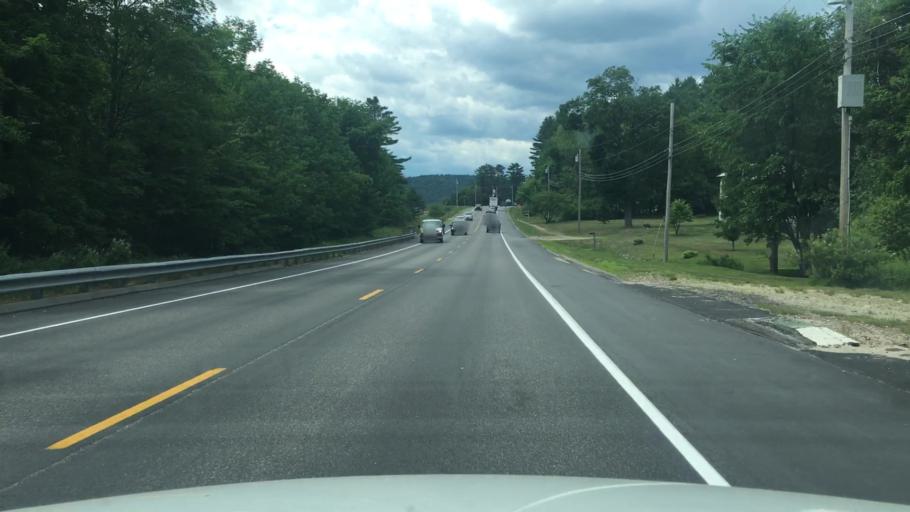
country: US
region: Maine
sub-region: Oxford County
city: Bethel
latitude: 44.4111
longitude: -70.7294
